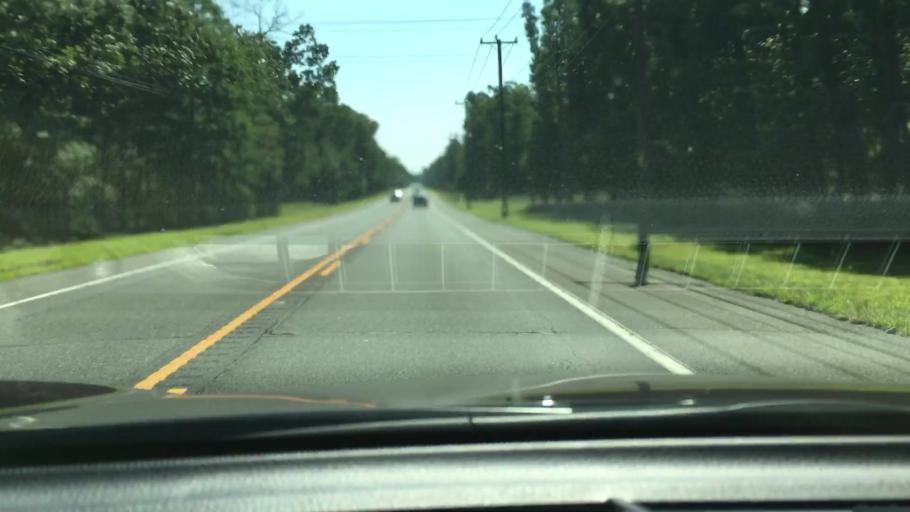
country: US
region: New Jersey
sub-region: Cumberland County
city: Laurel Lake
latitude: 39.3796
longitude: -74.9658
